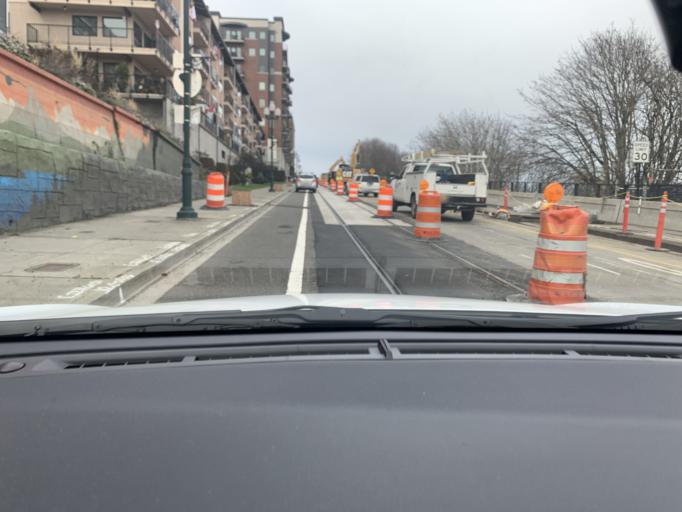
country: US
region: Washington
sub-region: Pierce County
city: Tacoma
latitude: 47.2587
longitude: -122.4410
